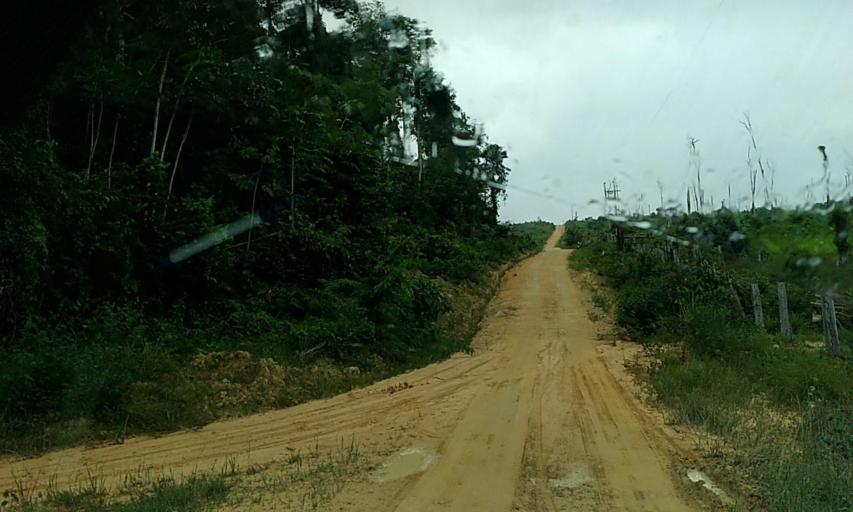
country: BR
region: Para
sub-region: Altamira
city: Altamira
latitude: -2.9539
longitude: -52.9009
